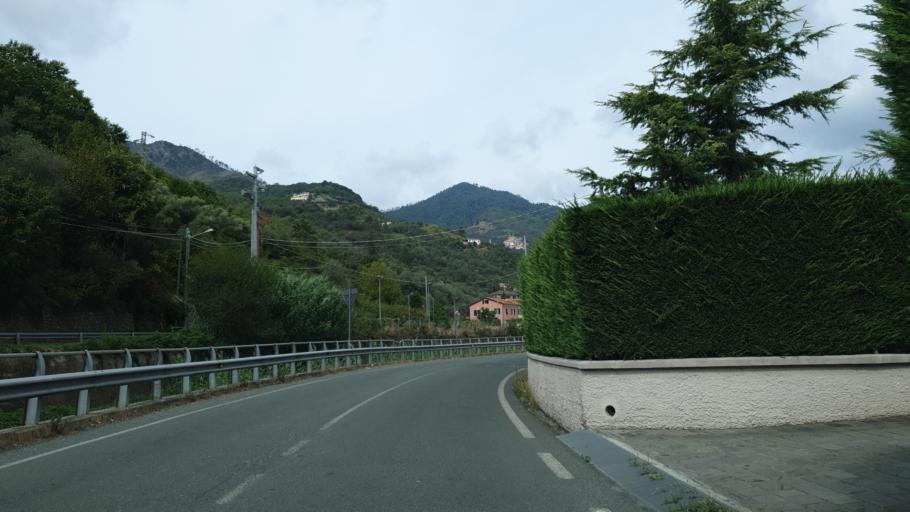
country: IT
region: Liguria
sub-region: Provincia di La Spezia
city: Levanto
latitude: 44.1803
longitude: 9.6224
